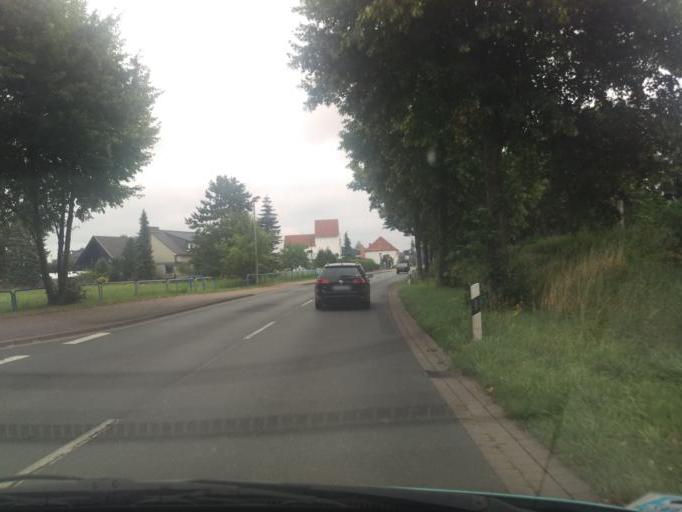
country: DE
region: Lower Saxony
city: Arpke
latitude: 52.3707
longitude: 10.1226
